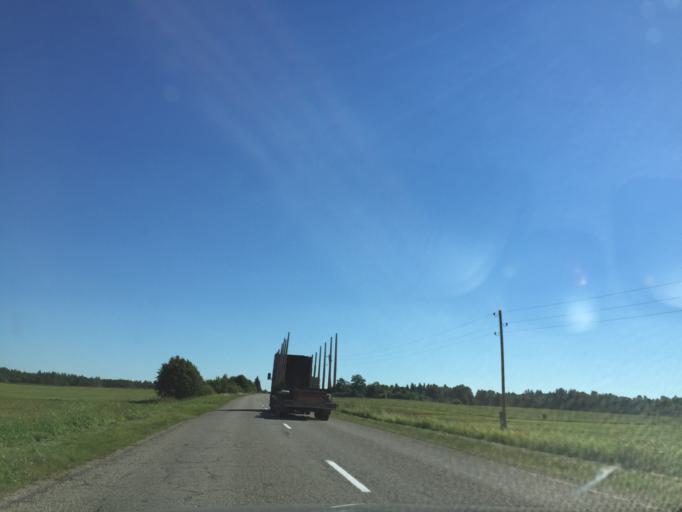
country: LV
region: Akniste
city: Akniste
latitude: 56.1029
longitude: 25.8591
